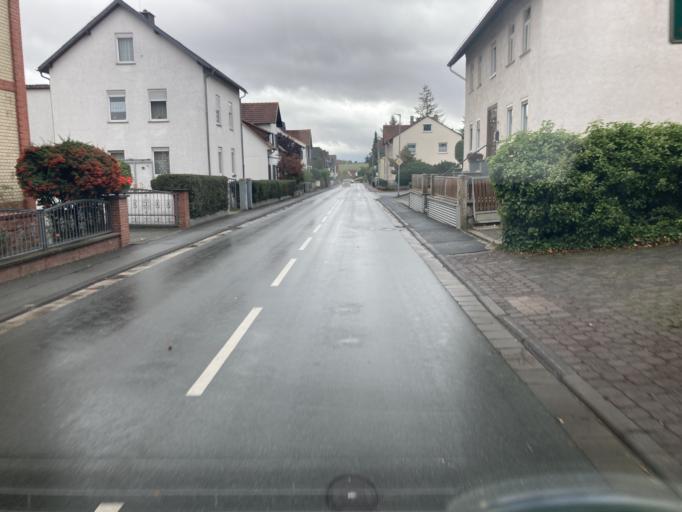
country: DE
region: Hesse
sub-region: Regierungsbezirk Darmstadt
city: Usingen
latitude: 50.3539
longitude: 8.5366
